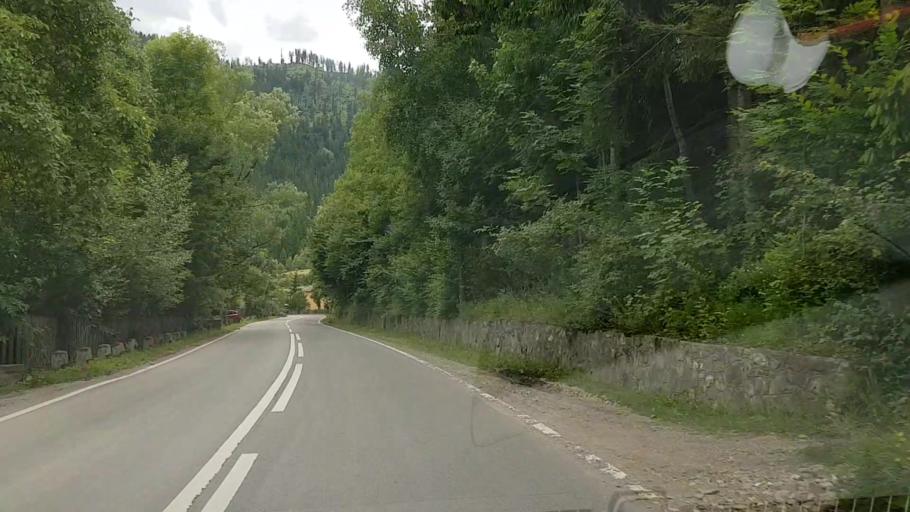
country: RO
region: Neamt
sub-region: Comuna Poiana Teiului
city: Poiana Teiului
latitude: 47.0976
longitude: 25.9418
